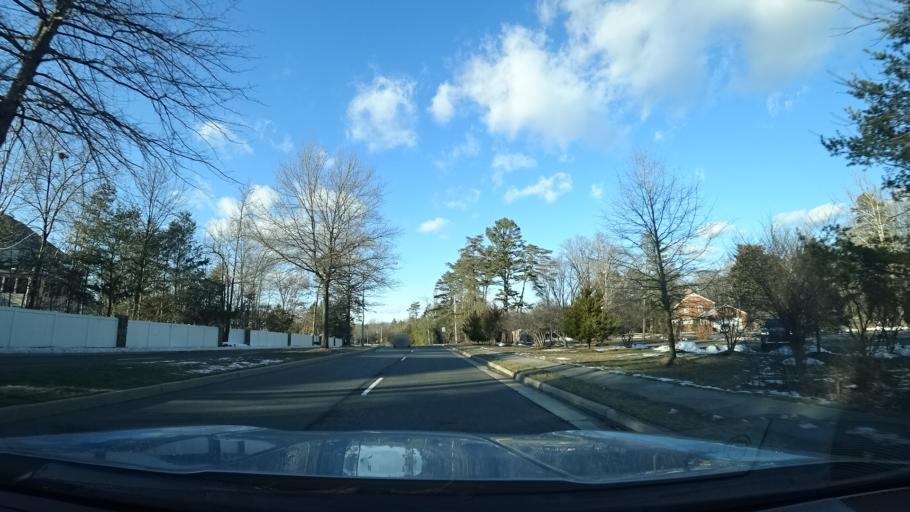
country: US
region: Virginia
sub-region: Fairfax County
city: Herndon
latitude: 38.9723
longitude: -77.3697
